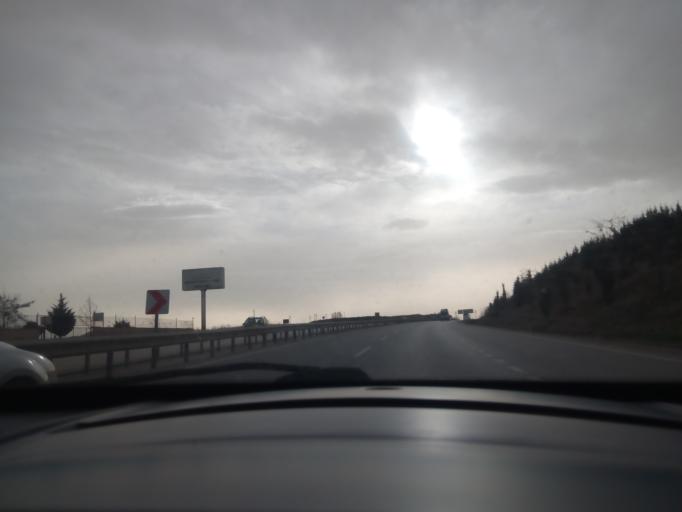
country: TR
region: Bursa
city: Tatkavakli
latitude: 40.0488
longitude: 28.3734
